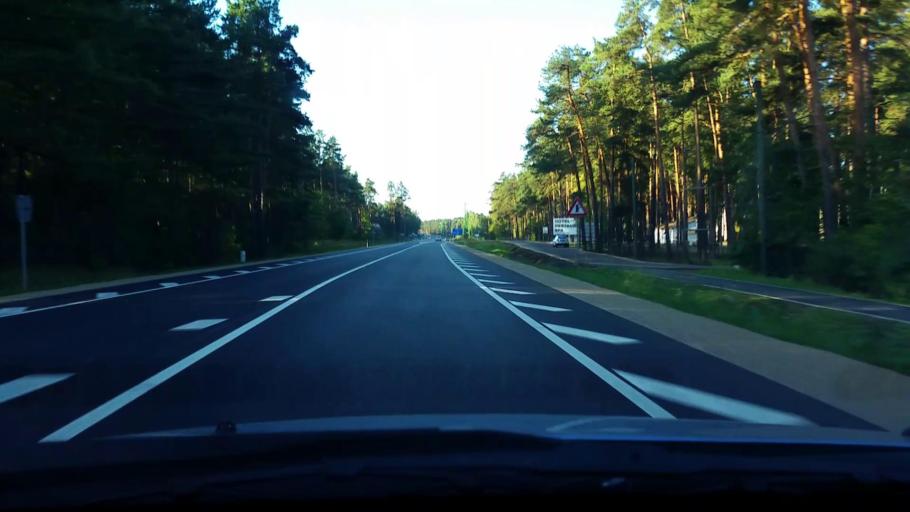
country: LV
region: Riga
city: Bergi
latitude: 57.0197
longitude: 24.3133
